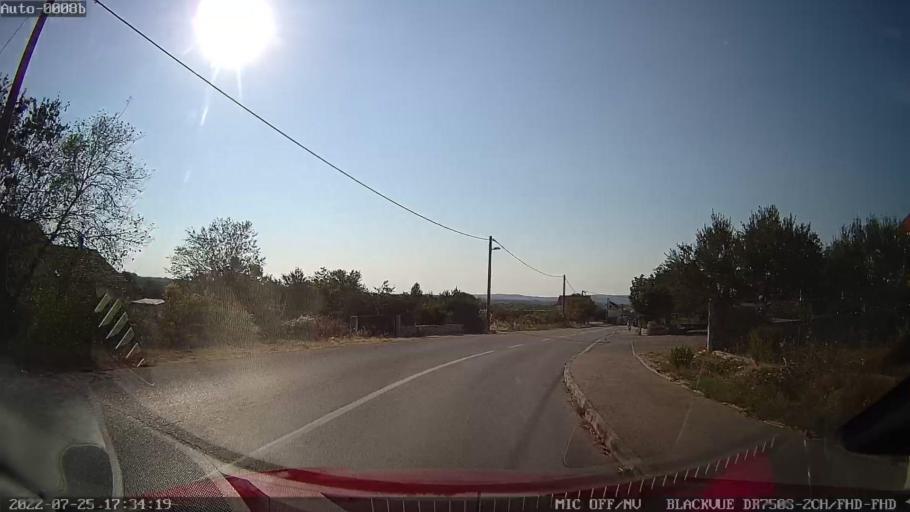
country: HR
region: Zadarska
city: Posedarje
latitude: 44.1833
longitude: 15.4784
